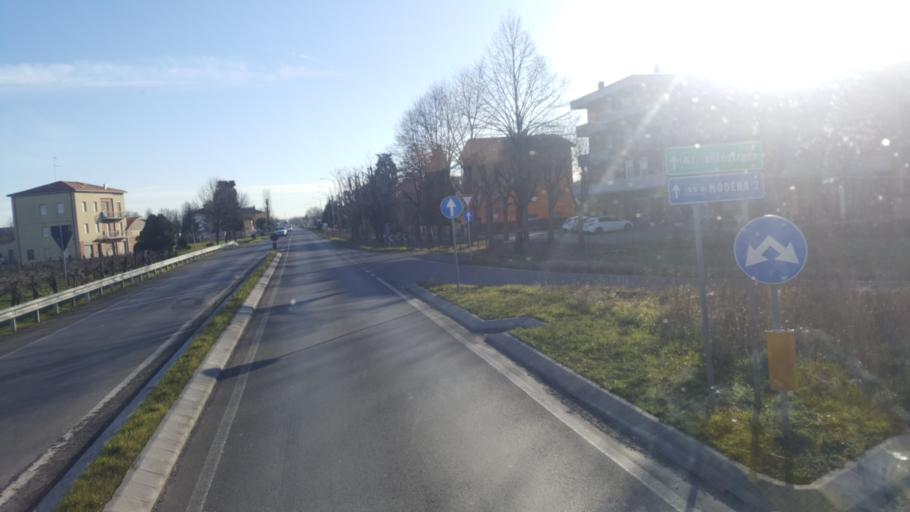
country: IT
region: Emilia-Romagna
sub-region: Provincia di Modena
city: Campogalliano
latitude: 44.6480
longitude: 10.8387
